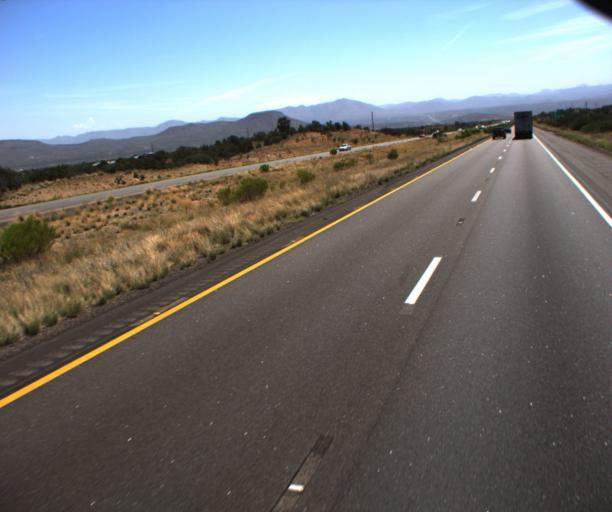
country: US
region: Arizona
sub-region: Mohave County
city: New Kingman-Butler
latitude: 35.1648
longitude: -113.7353
